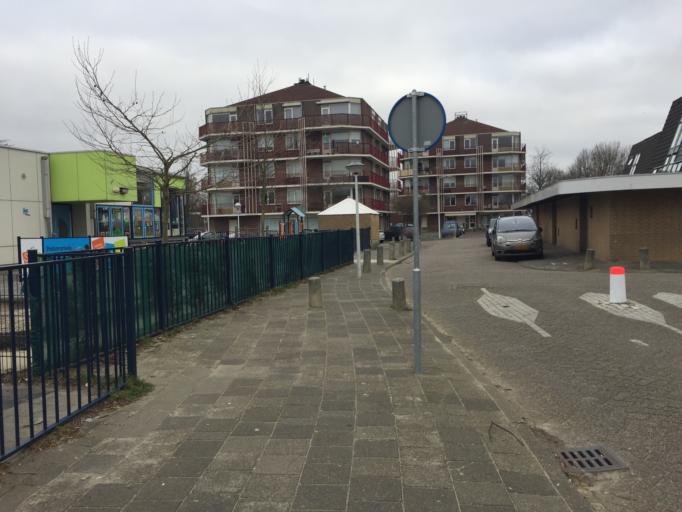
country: NL
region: South Holland
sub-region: Gemeente Leiden
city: Leiden
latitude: 52.1795
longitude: 4.5033
